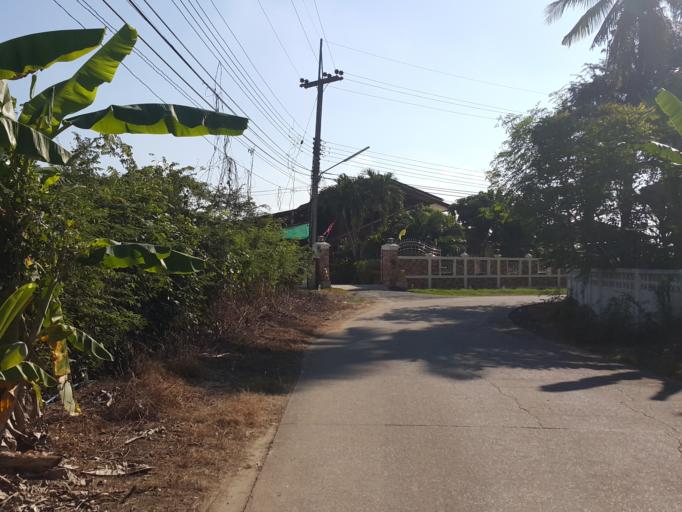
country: TH
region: Chiang Mai
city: Mae On
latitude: 18.7995
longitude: 99.1755
